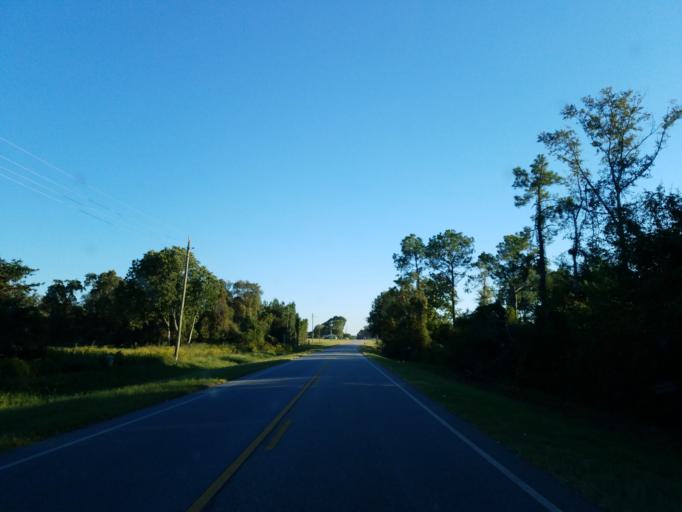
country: US
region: Georgia
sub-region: Worth County
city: Sylvester
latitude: 31.6281
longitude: -83.8654
